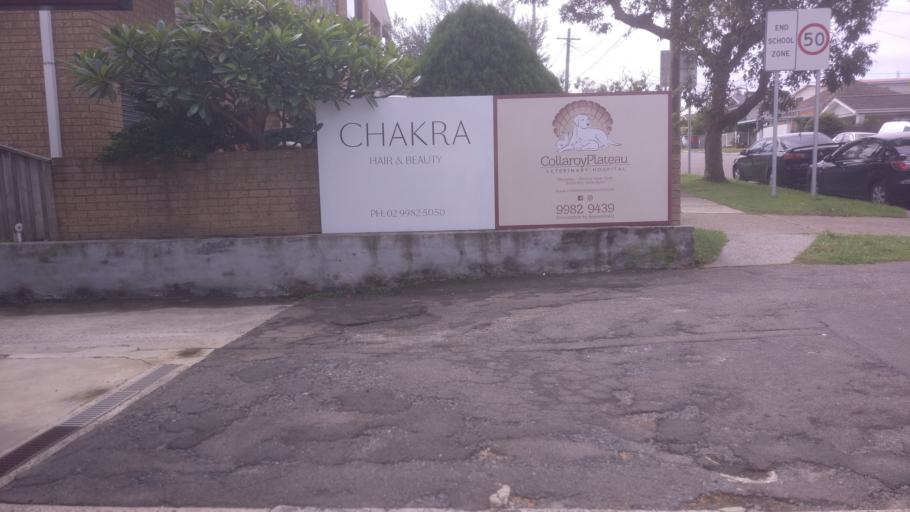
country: AU
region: New South Wales
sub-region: Warringah
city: Narrabeen
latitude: -33.7306
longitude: 151.2925
